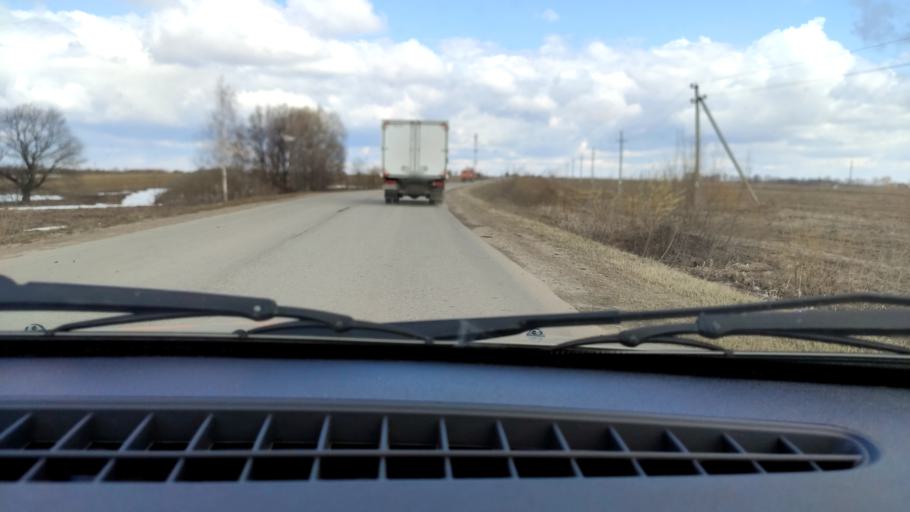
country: RU
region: Bashkortostan
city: Kudeyevskiy
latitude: 54.8343
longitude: 56.7929
